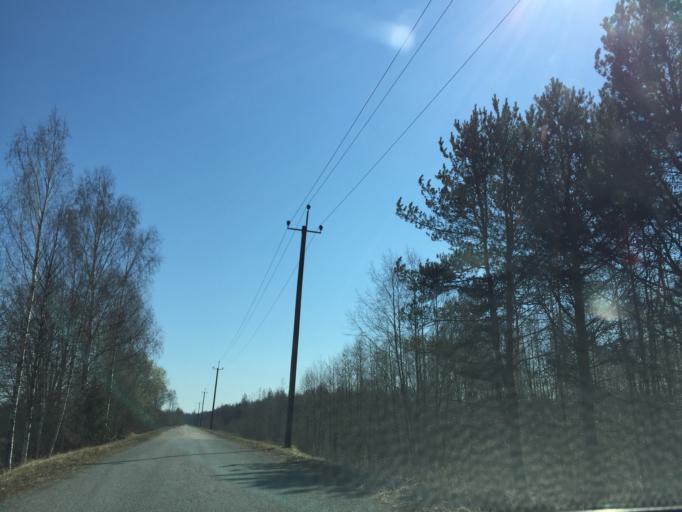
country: EE
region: Jogevamaa
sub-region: Mustvee linn
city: Mustvee
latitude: 58.7801
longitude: 26.9360
